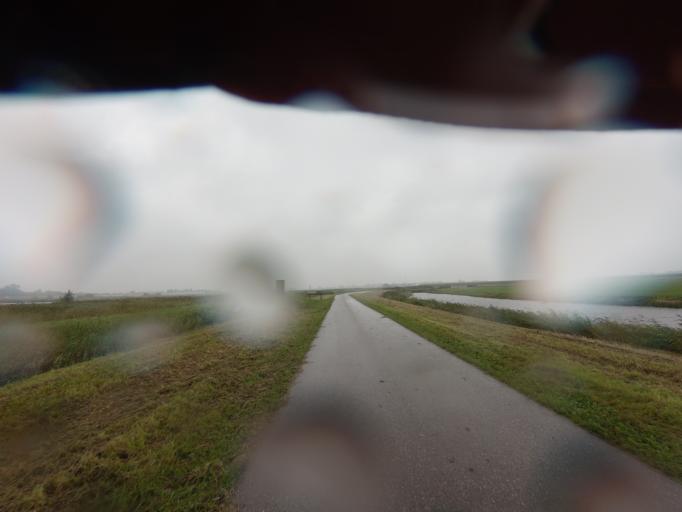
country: NL
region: North Holland
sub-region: Gemeente Medemblik
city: Opperdoes
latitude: 52.7530
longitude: 5.0578
